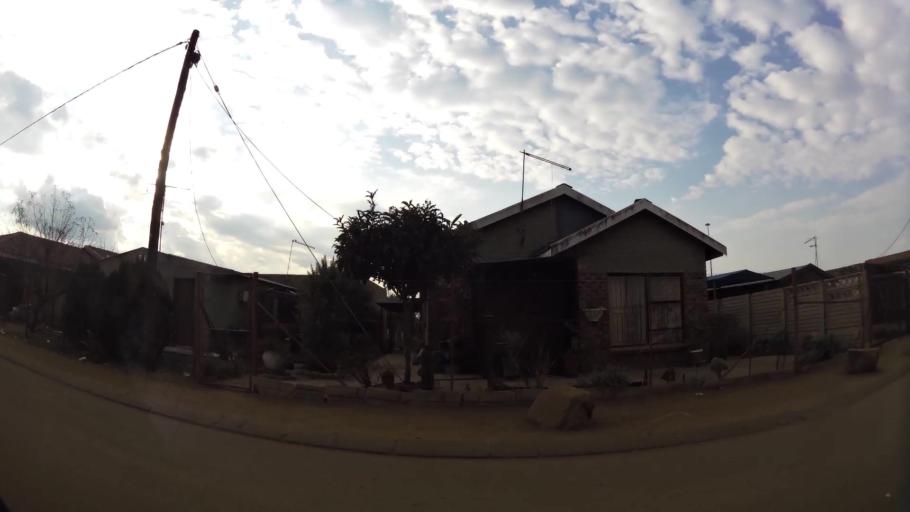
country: ZA
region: Gauteng
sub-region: Sedibeng District Municipality
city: Vanderbijlpark
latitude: -26.6752
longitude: 27.8711
